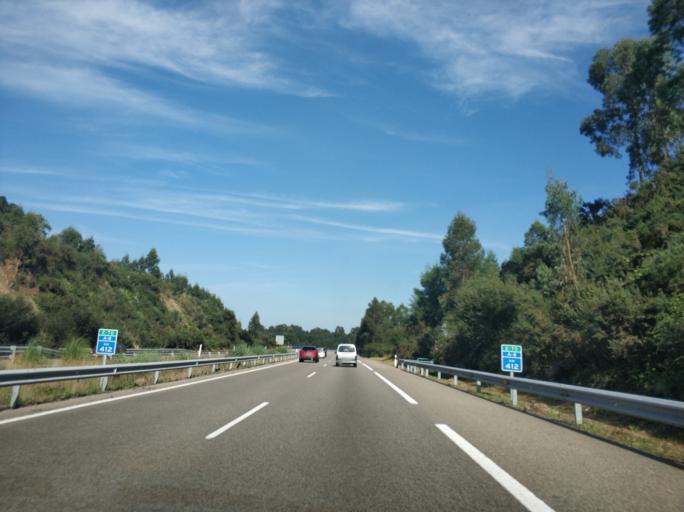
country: ES
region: Asturias
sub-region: Province of Asturias
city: Castrillon
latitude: 43.5485
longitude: -5.9808
